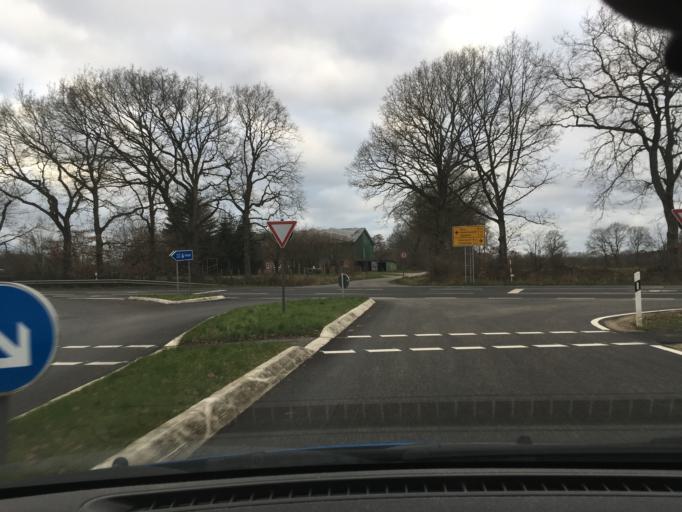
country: DE
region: Schleswig-Holstein
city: Schafstedt
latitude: 54.0752
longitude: 9.2912
